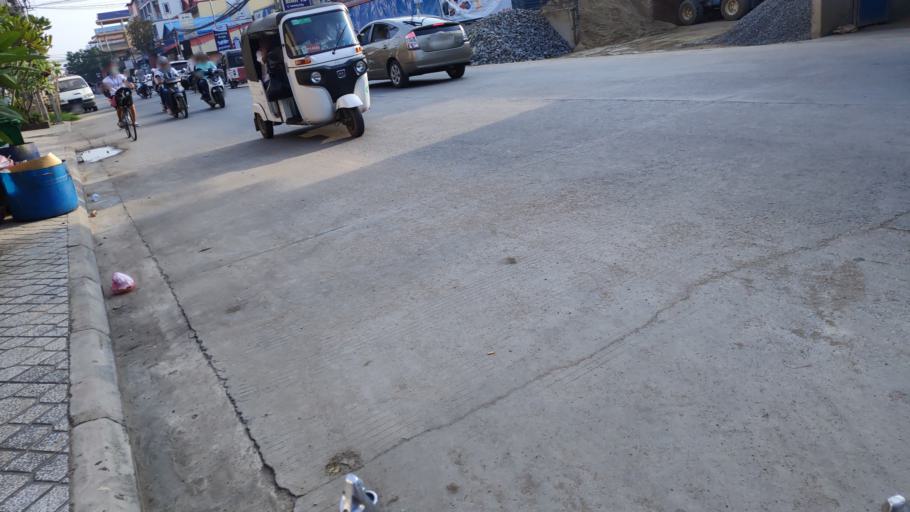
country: KH
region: Phnom Penh
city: Phnom Penh
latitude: 11.5495
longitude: 104.8859
